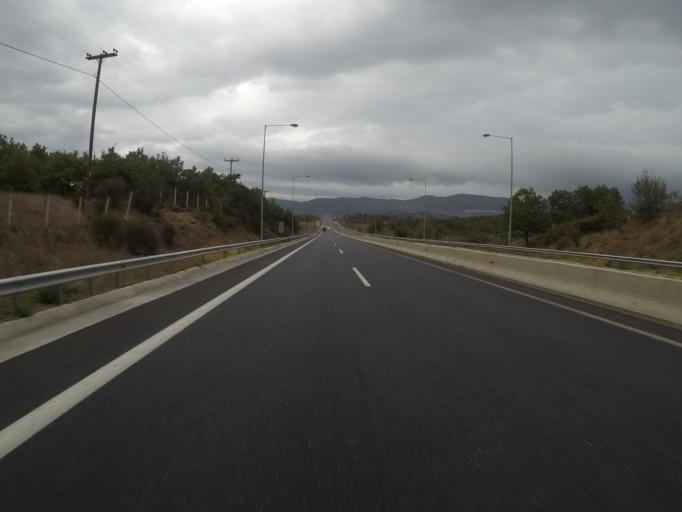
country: GR
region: Peloponnese
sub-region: Nomos Arkadias
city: Megalopoli
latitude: 37.3654
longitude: 22.1521
